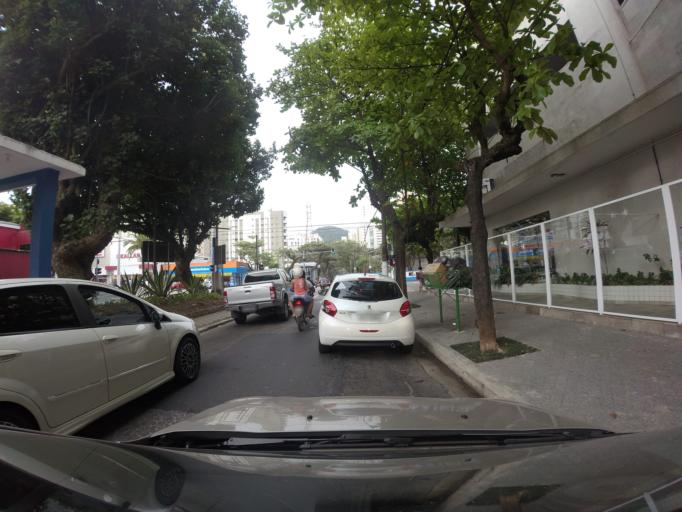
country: BR
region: Sao Paulo
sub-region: Guaruja
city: Guaruja
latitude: -23.9950
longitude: -46.2572
